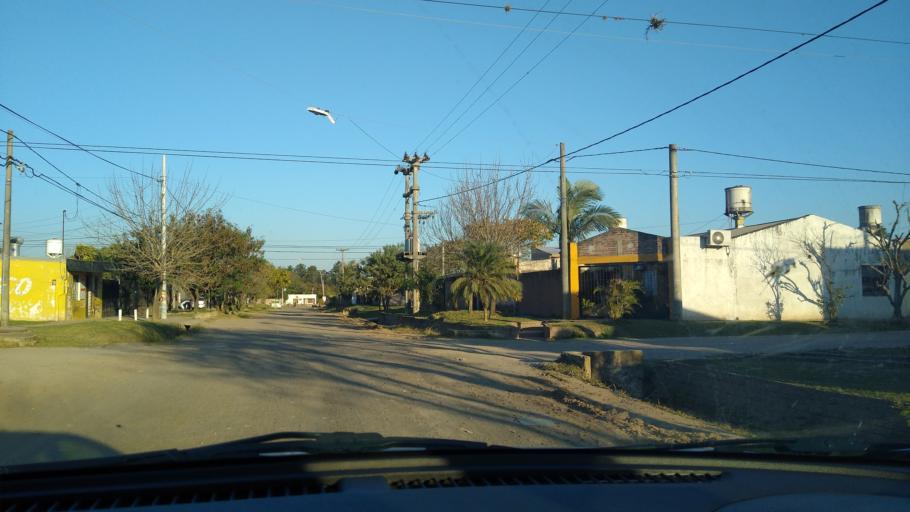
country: AR
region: Chaco
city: Resistencia
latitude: -27.4893
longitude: -58.9747
